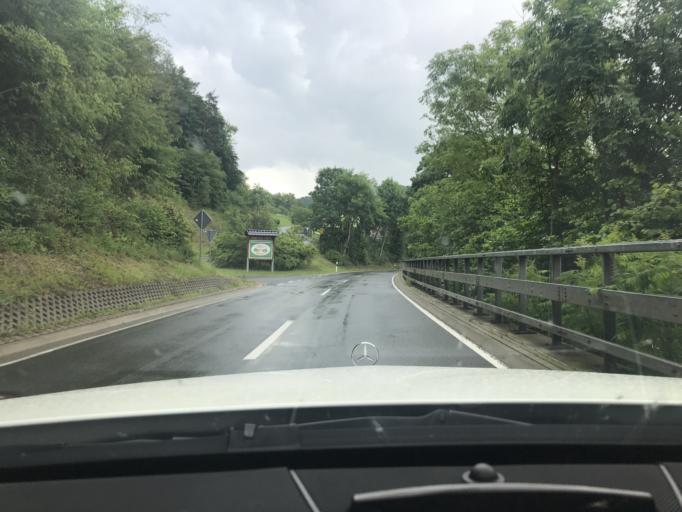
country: DE
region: Thuringia
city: Heyerode
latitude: 51.1651
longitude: 10.3130
